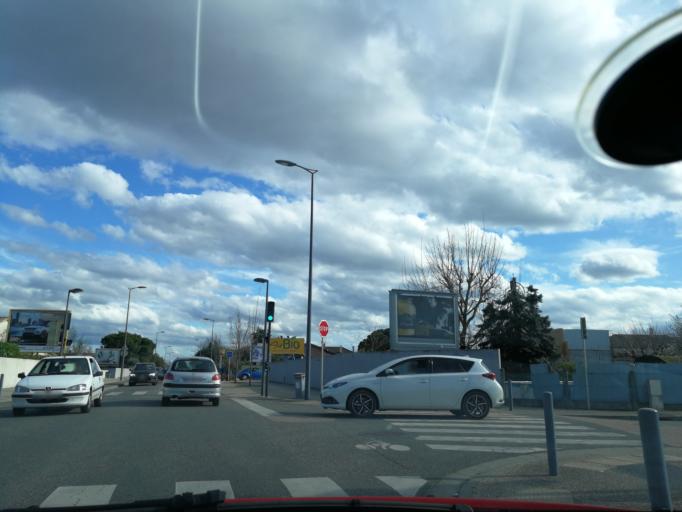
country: FR
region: Midi-Pyrenees
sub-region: Departement de la Haute-Garonne
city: Blagnac
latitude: 43.6459
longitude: 1.3846
